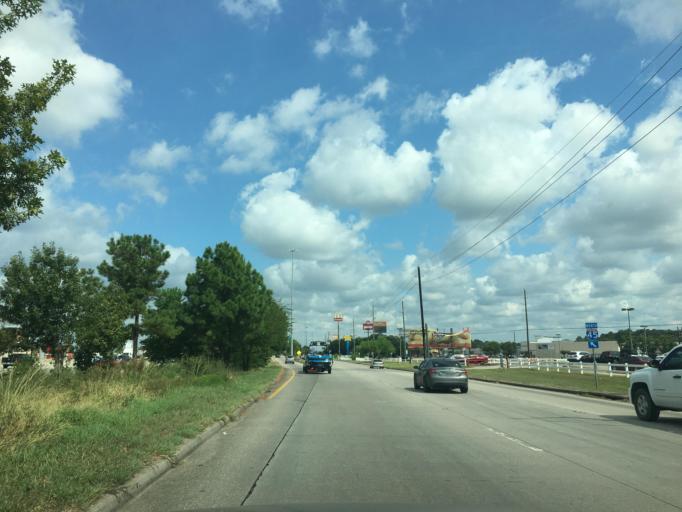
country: US
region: Texas
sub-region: Harris County
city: Spring
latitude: 30.0695
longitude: -95.4345
